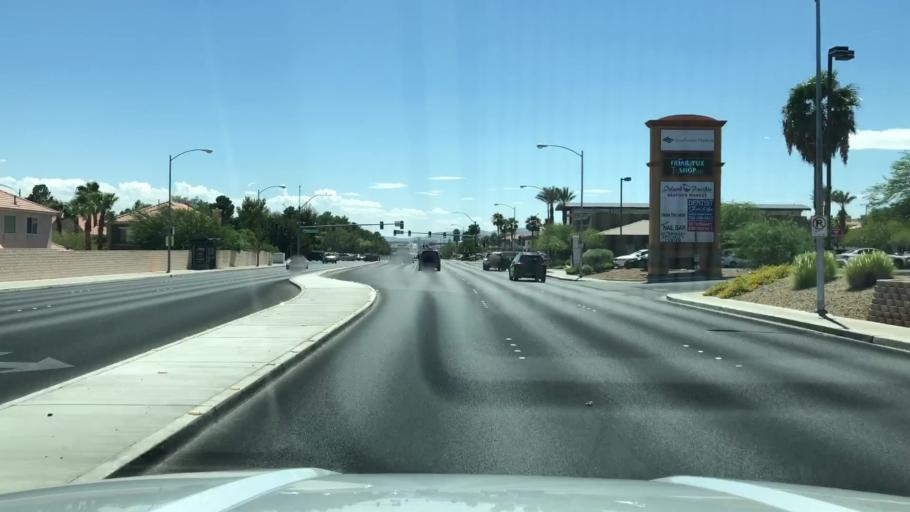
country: US
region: Nevada
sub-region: Clark County
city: Spring Valley
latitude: 36.1014
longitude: -115.2793
